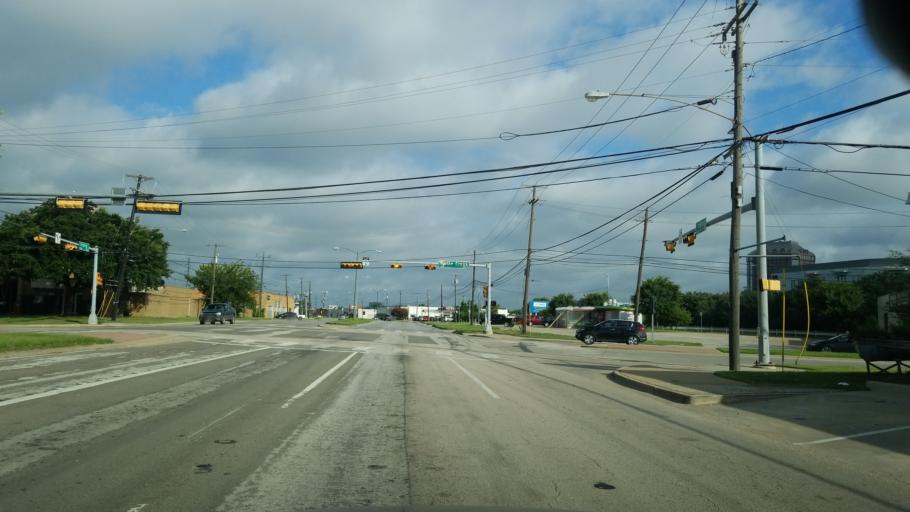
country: US
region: Texas
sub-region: Dallas County
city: Dallas
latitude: 32.7940
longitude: -96.8260
